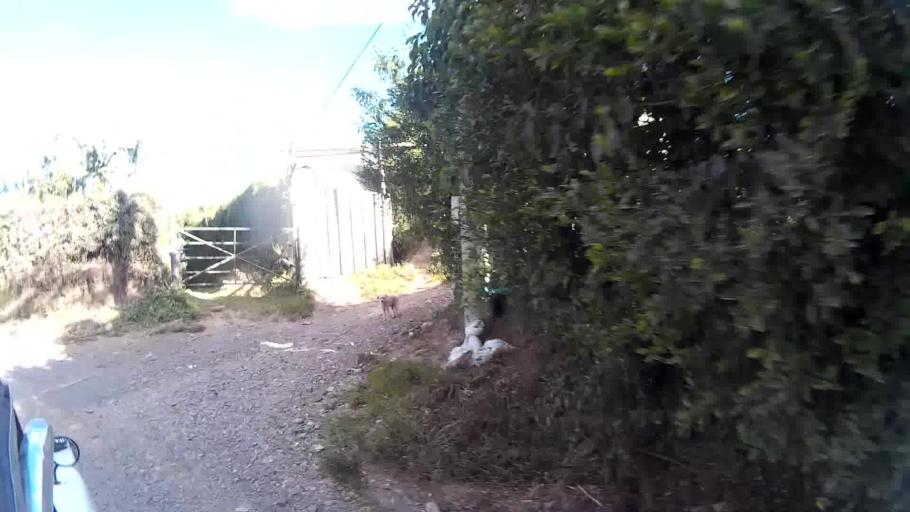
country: CO
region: Quindio
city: Filandia
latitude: 4.7195
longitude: -75.6833
